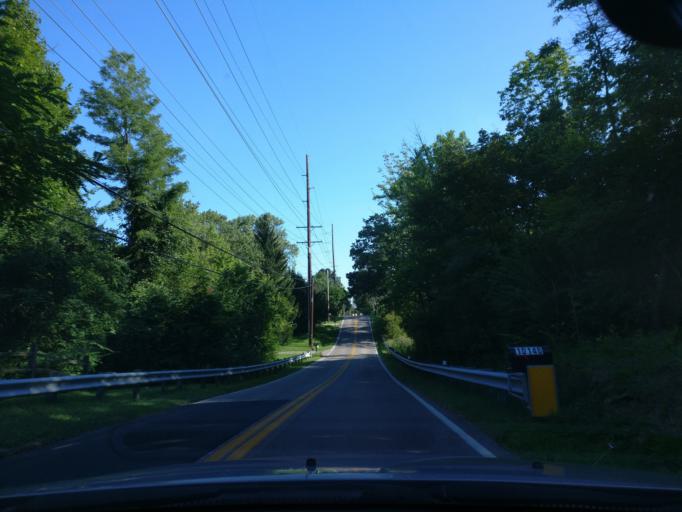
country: US
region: Ohio
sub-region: Warren County
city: Five Points
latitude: 39.6023
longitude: -84.2093
